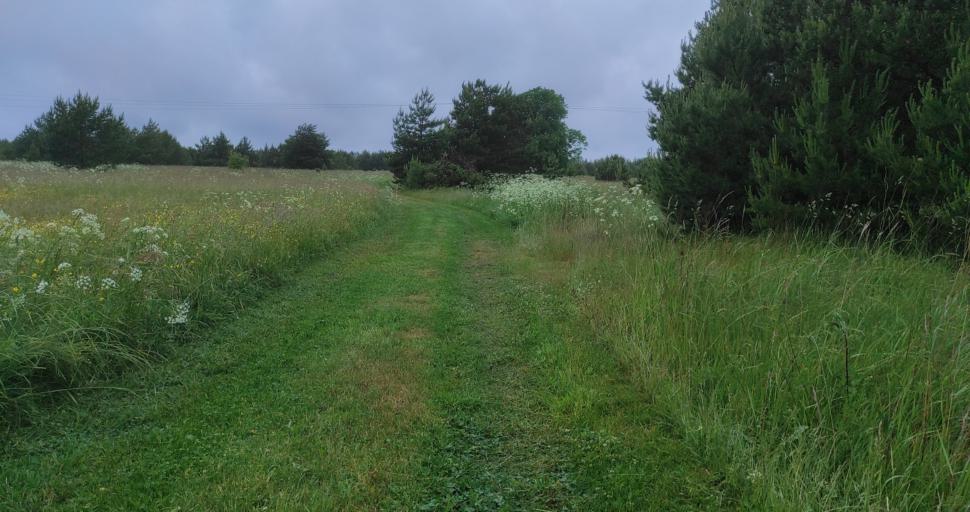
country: LV
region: Pavilostas
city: Pavilosta
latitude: 56.9558
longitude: 21.3159
